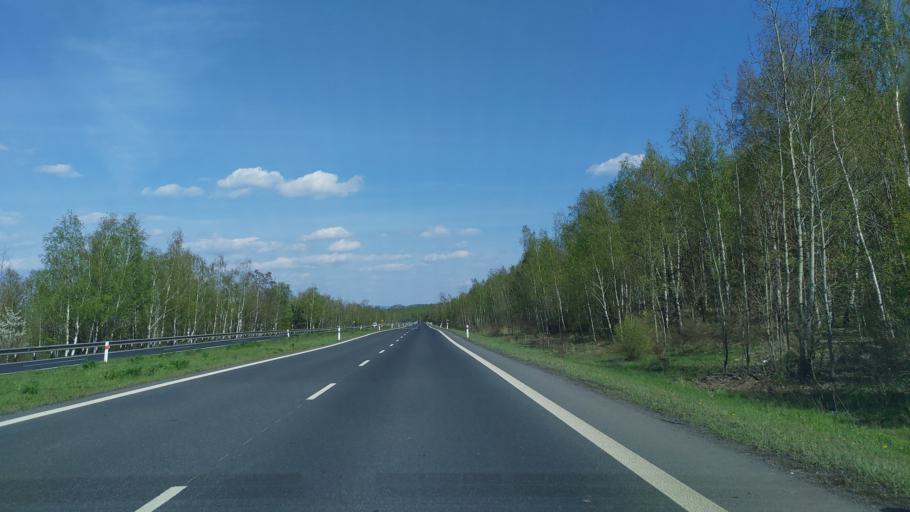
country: CZ
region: Ustecky
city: Jirkov
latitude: 50.5120
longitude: 13.5005
